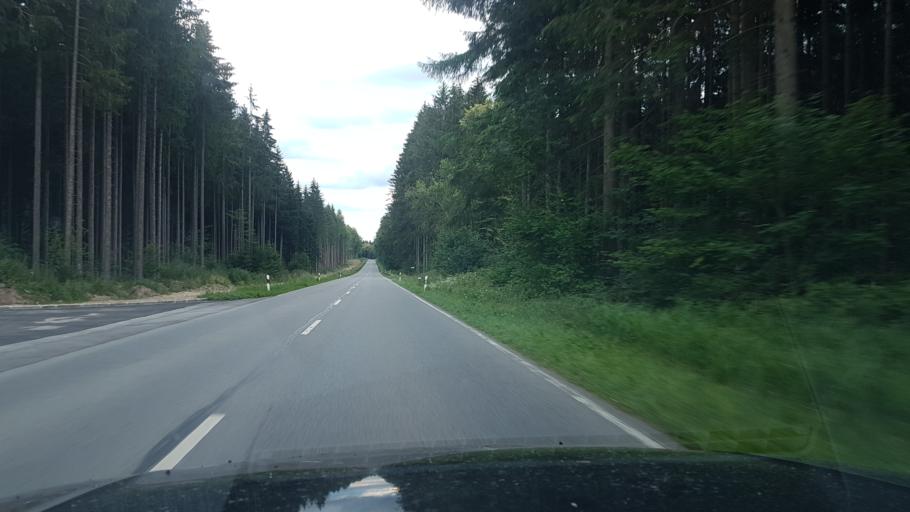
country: DE
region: Baden-Wuerttemberg
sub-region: Freiburg Region
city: Braunlingen
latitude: 47.9614
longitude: 8.4501
